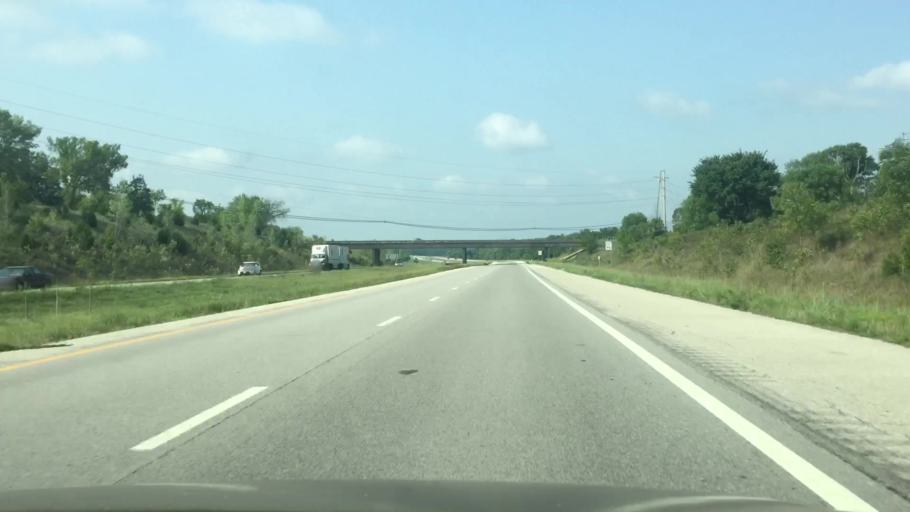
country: US
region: Kansas
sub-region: Miami County
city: Paola
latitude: 38.5644
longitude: -94.8596
